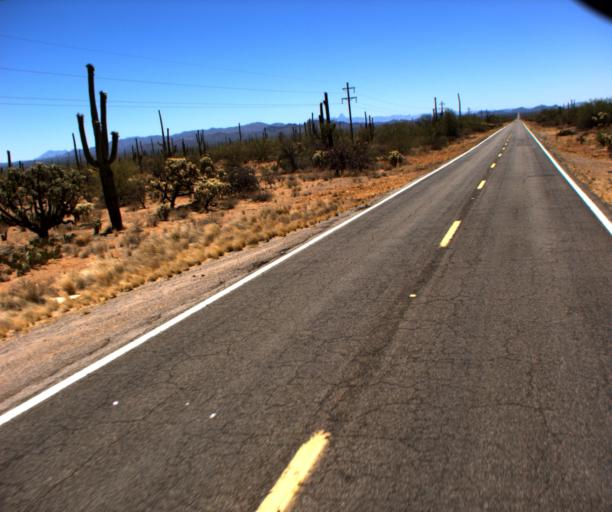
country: US
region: Arizona
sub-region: Pima County
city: Sells
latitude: 32.1173
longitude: -112.0793
